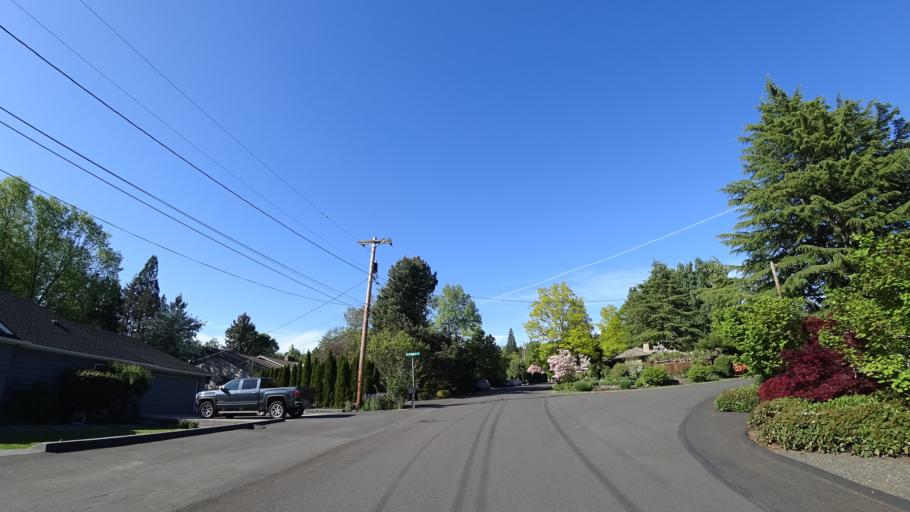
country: US
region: Oregon
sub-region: Washington County
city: West Slope
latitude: 45.4941
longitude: -122.7635
